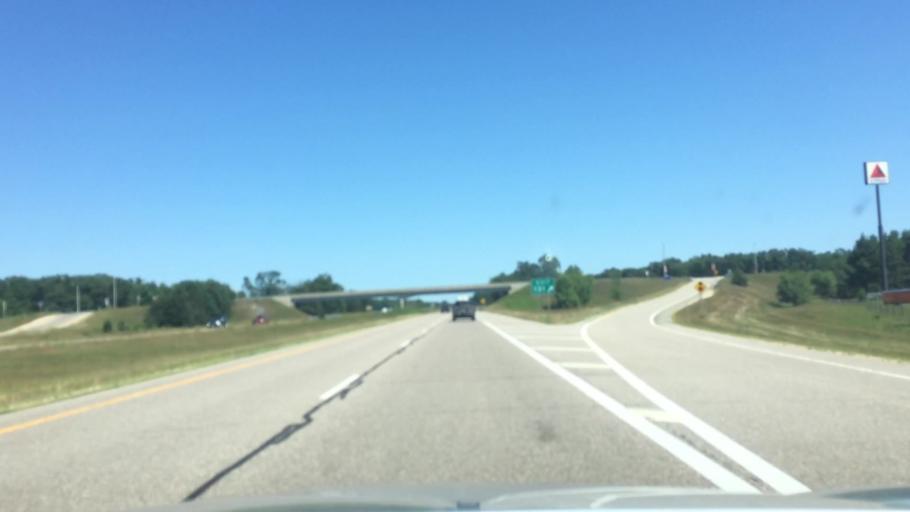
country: US
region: Wisconsin
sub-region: Marquette County
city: Westfield
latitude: 44.1314
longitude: -89.5323
